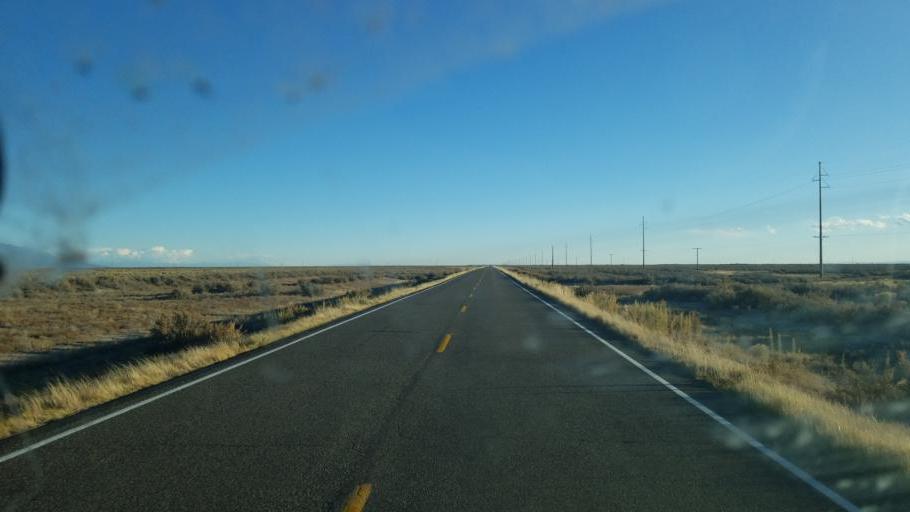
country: US
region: Colorado
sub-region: Saguache County
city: Center
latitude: 37.9288
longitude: -105.9007
